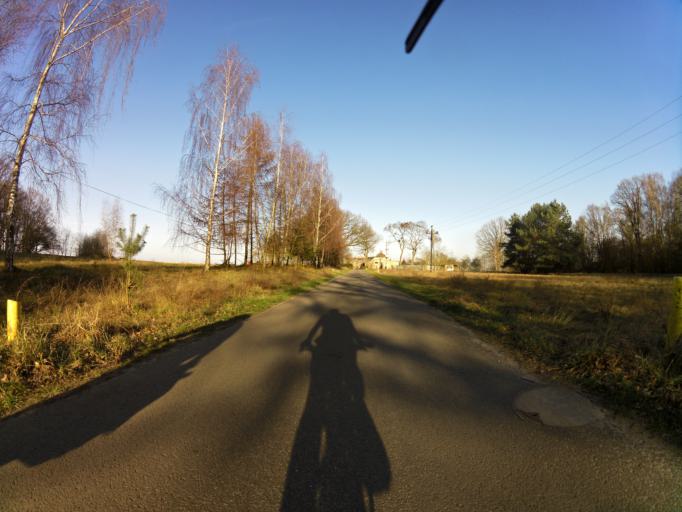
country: PL
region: West Pomeranian Voivodeship
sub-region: Powiat policki
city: Nowe Warpno
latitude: 53.7326
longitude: 14.3287
